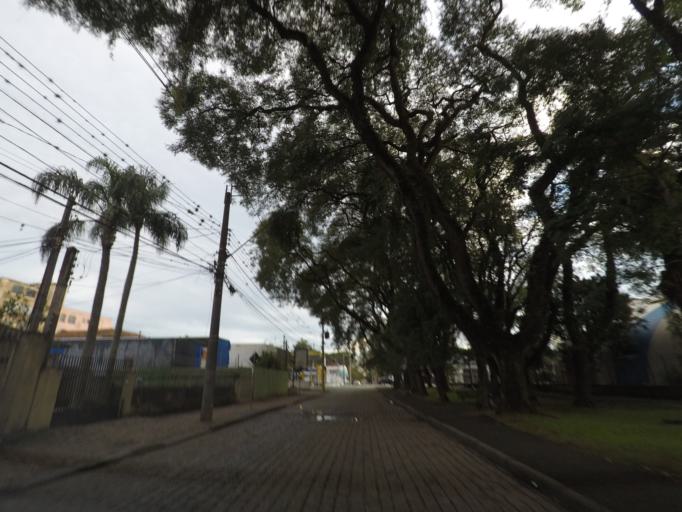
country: BR
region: Parana
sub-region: Curitiba
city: Curitiba
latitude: -25.4262
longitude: -49.2501
